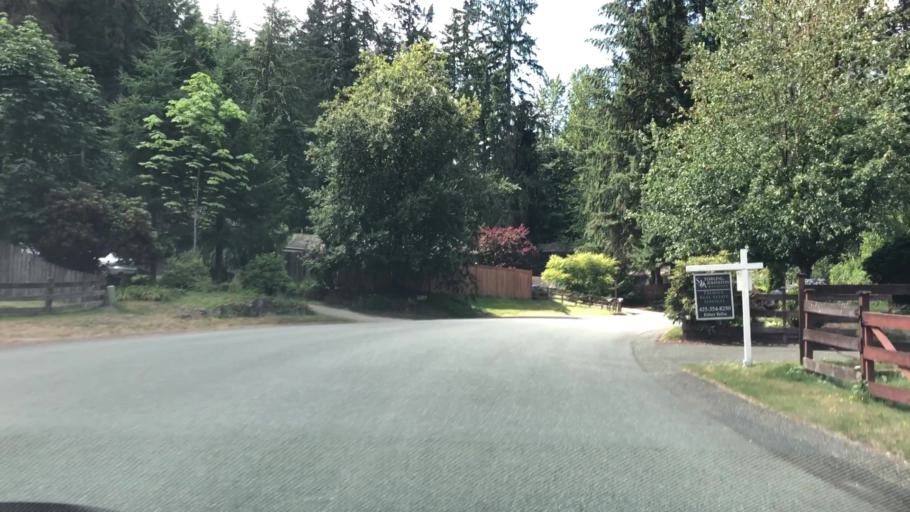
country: US
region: Washington
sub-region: King County
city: Cottage Lake
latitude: 47.7403
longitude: -122.1078
